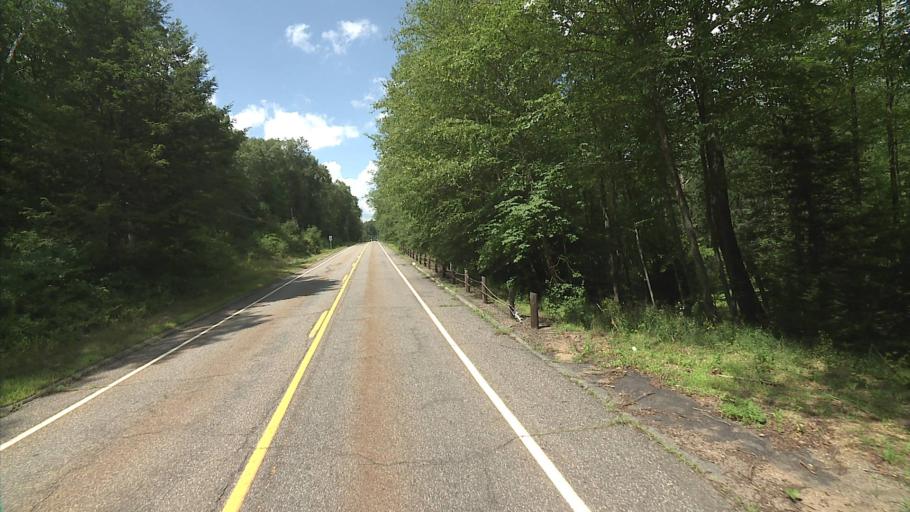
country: US
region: Connecticut
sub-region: Tolland County
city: Stafford
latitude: 41.9622
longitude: -72.1979
